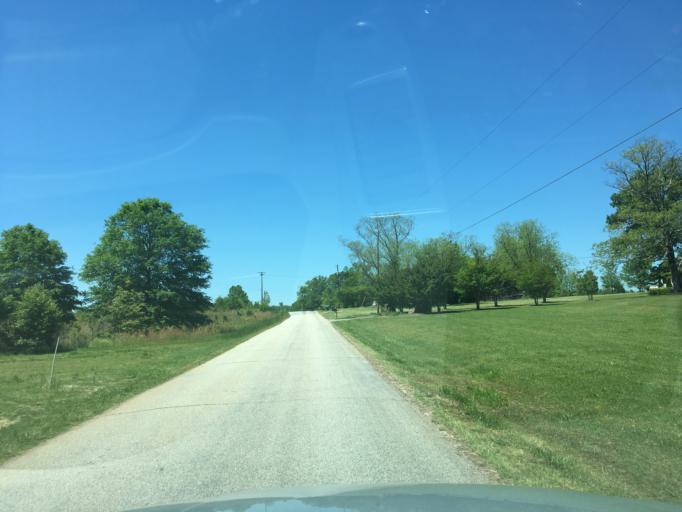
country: US
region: South Carolina
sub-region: Spartanburg County
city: Duncan
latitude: 34.8824
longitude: -82.1824
